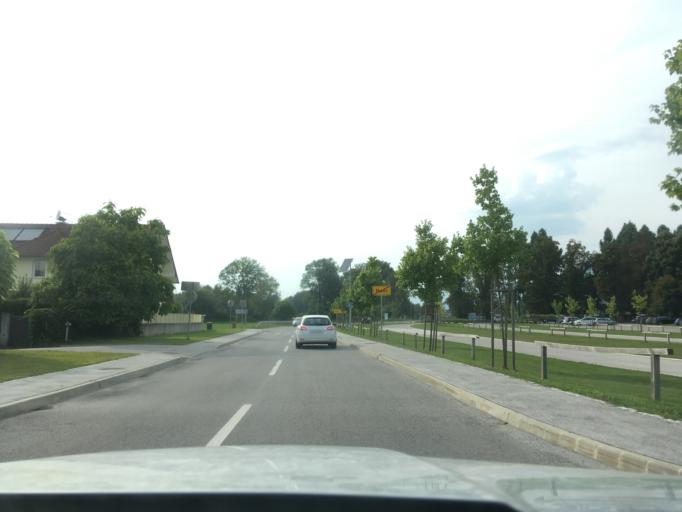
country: SI
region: Domzale
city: Radomlje
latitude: 46.1836
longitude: 14.6076
